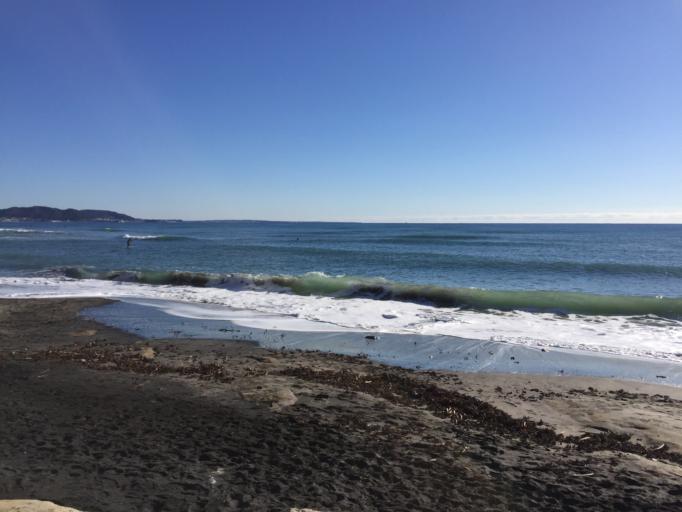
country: JP
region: Kanagawa
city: Kamakura
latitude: 35.3033
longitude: 139.5222
